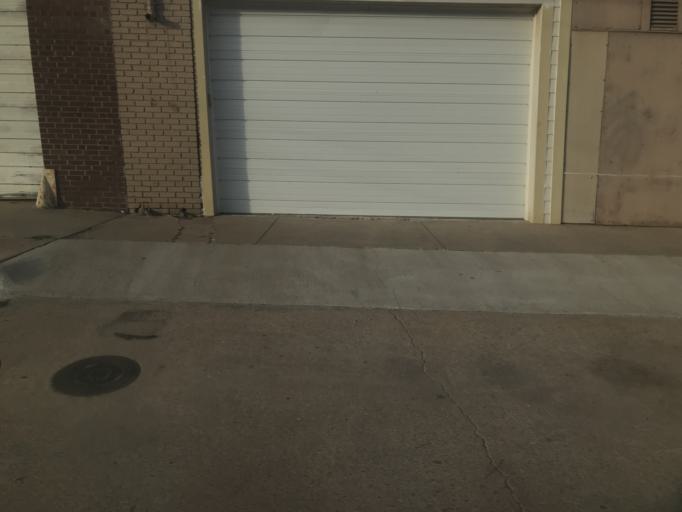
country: US
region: Texas
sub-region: Taylor County
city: Abilene
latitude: 32.4322
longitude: -99.7413
